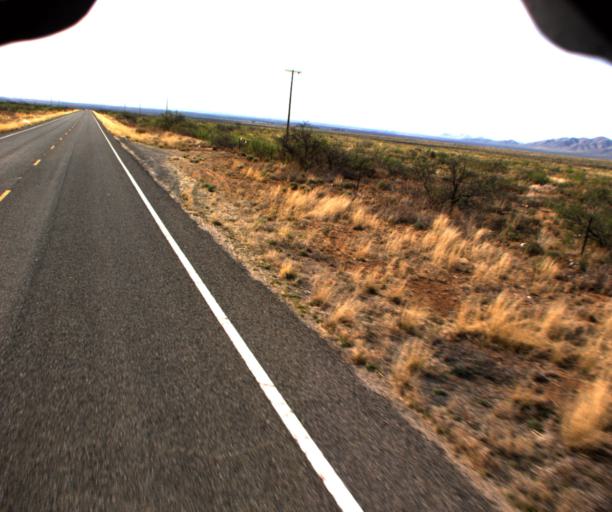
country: US
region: Arizona
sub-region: Cochise County
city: Willcox
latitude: 32.1874
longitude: -109.6811
